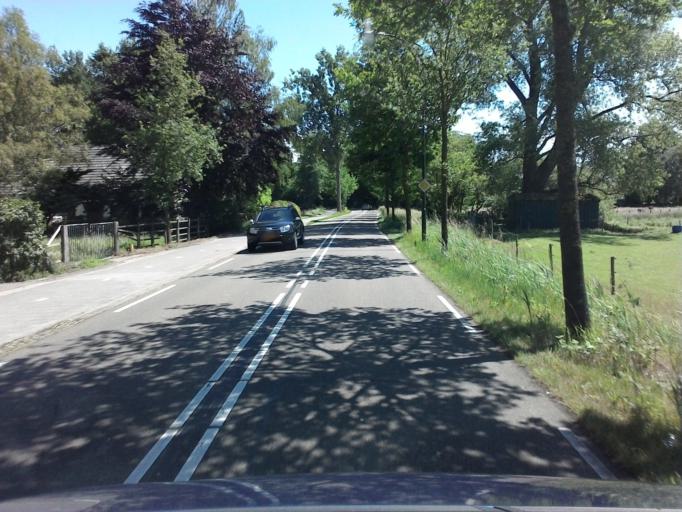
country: NL
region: North Brabant
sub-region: Gemeente Sint-Michielsgestel
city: Sint-Michielsgestel
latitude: 51.6379
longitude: 5.3695
